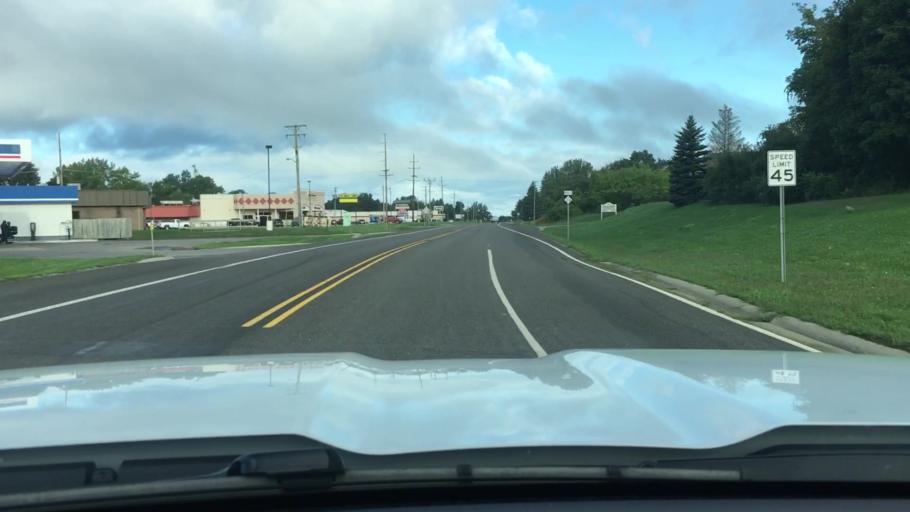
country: US
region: Michigan
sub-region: Lapeer County
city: Barnes Lake-Millers Lake
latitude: 43.3372
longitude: -83.3453
